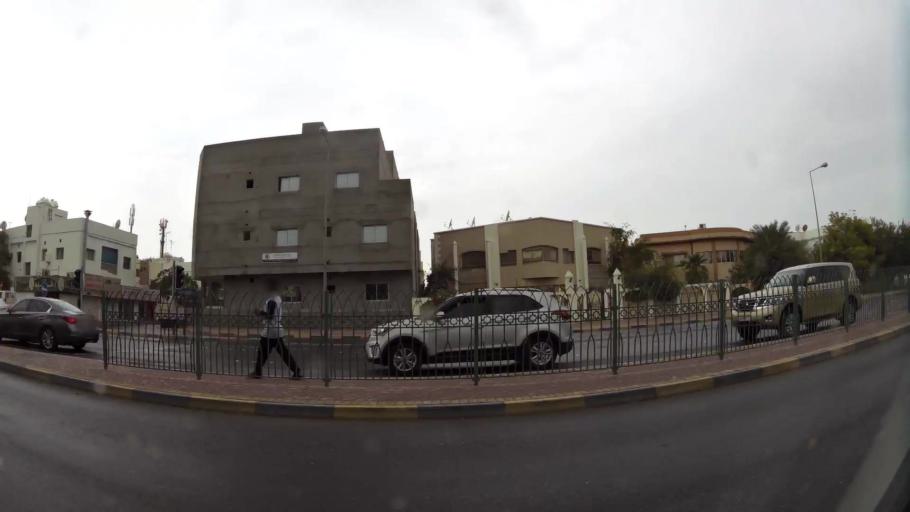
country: BH
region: Northern
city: Ar Rifa'
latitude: 26.1302
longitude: 50.5655
